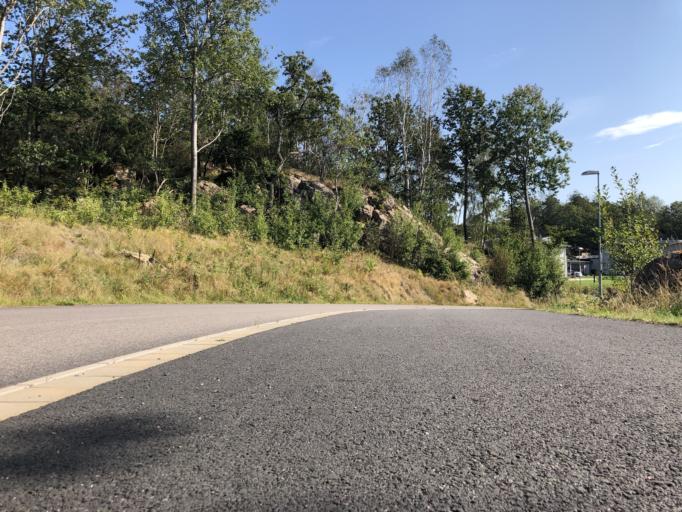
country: SE
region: Vaestra Goetaland
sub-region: Goteborg
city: Goeteborg
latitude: 57.7423
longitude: 11.9607
